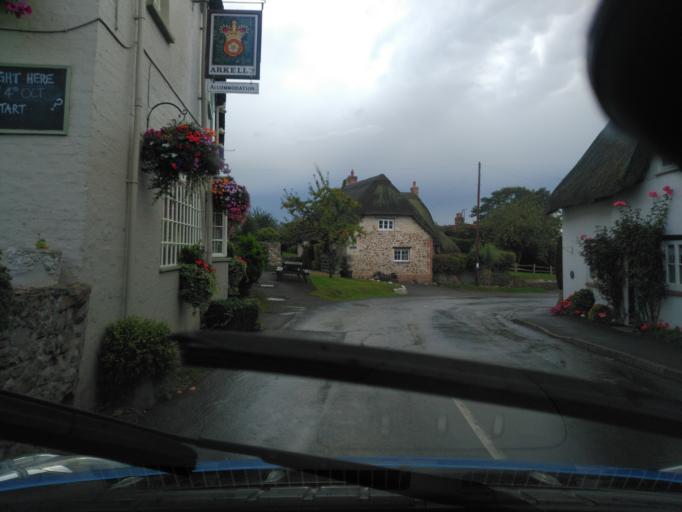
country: GB
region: England
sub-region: Borough of Swindon
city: Bishopstone
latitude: 51.5637
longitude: -1.6194
